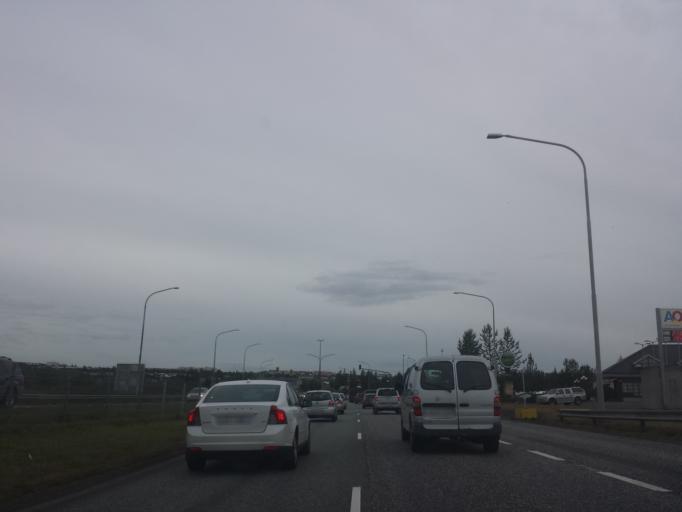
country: IS
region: Capital Region
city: Reykjavik
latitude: 64.1215
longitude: -21.8474
